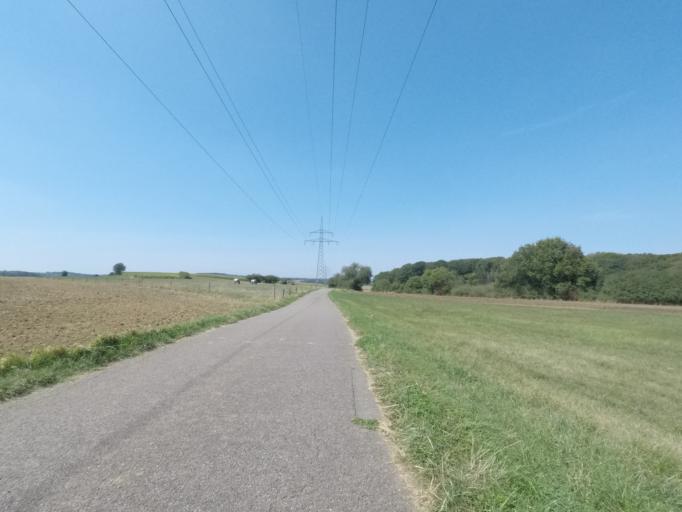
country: LU
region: Luxembourg
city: Capellen
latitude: 49.6233
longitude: 5.9960
